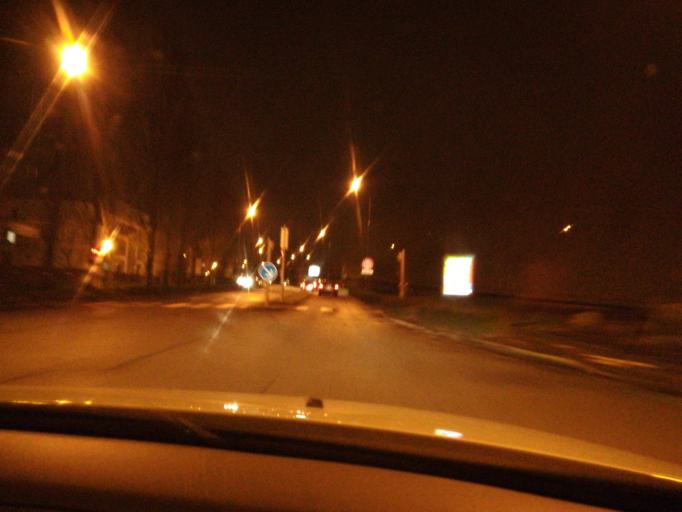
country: FR
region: Haute-Normandie
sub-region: Departement de la Seine-Maritime
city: Bois-Guillaume
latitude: 49.4692
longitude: 1.1268
